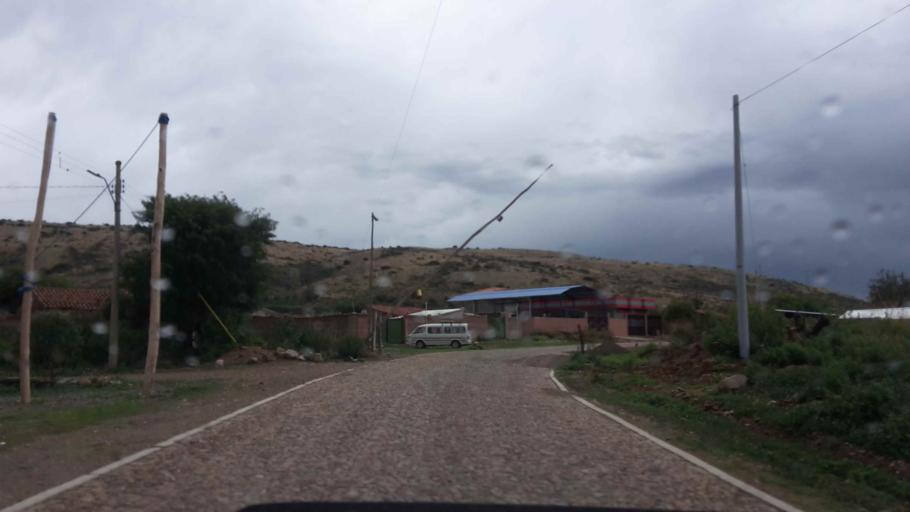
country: BO
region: Cochabamba
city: Cochabamba
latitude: -17.5487
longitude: -66.1816
